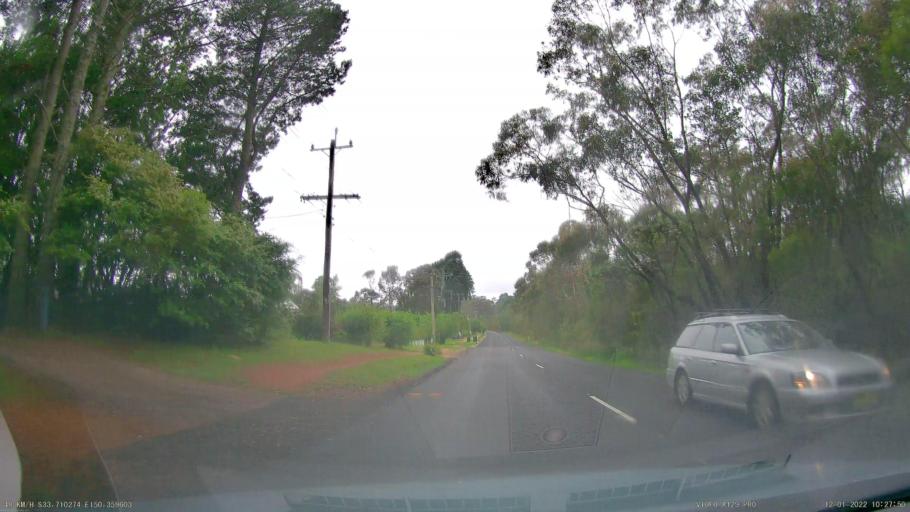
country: AU
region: New South Wales
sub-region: Blue Mountains Municipality
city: Leura
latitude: -33.7103
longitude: 150.3599
